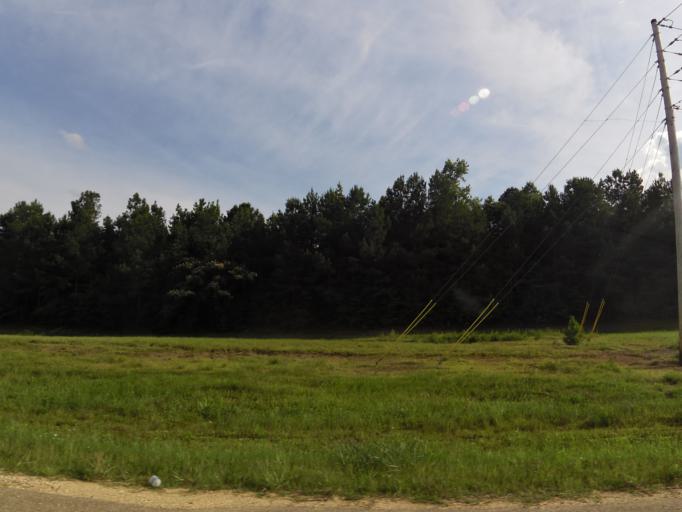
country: US
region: Tennessee
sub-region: Benton County
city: Camden
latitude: 36.0404
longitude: -88.1320
